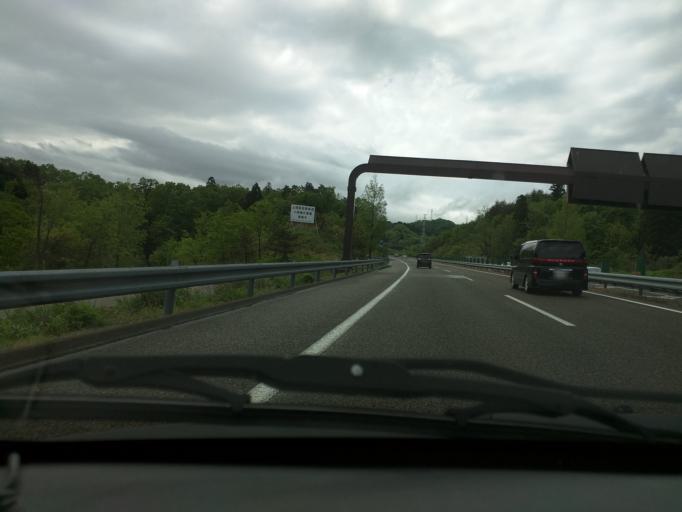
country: JP
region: Niigata
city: Joetsu
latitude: 37.1360
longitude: 138.2137
